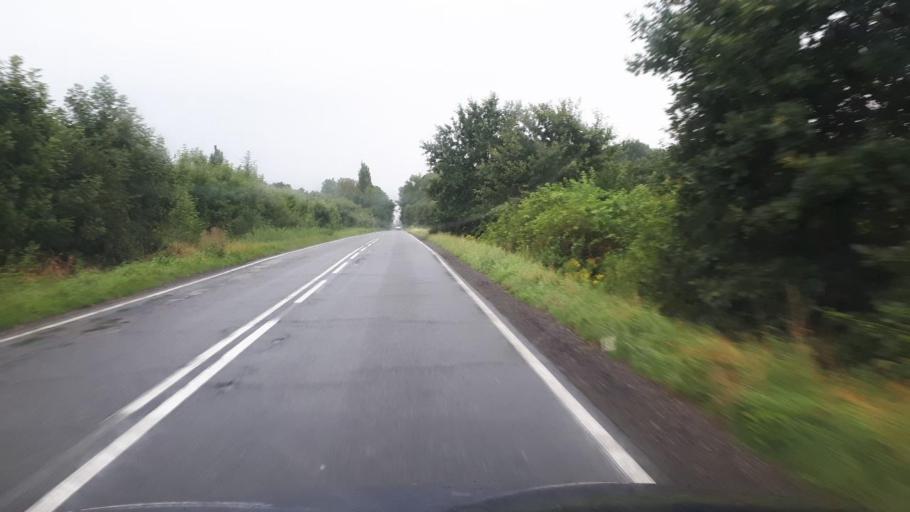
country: PL
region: Silesian Voivodeship
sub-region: Powiat tarnogorski
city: Wieszowa
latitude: 50.3445
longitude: 18.7157
